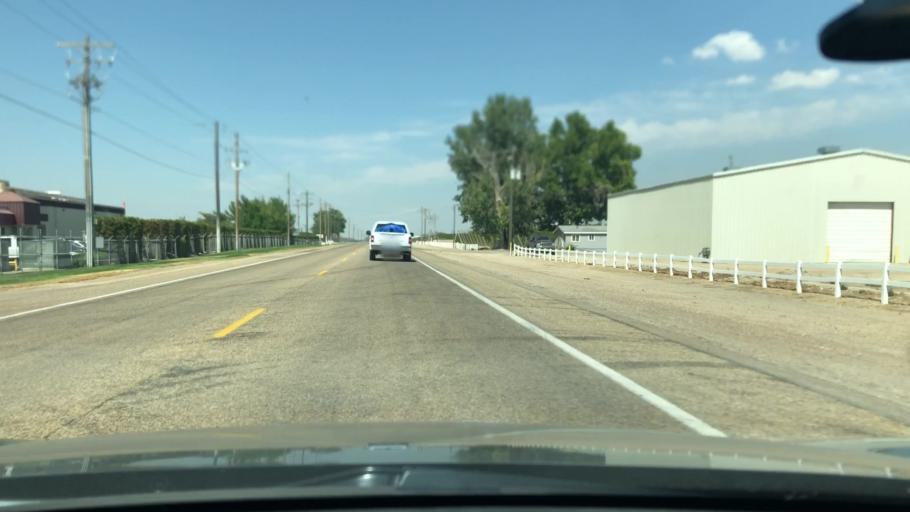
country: US
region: Idaho
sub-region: Canyon County
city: Wilder
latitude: 43.6949
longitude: -116.9120
